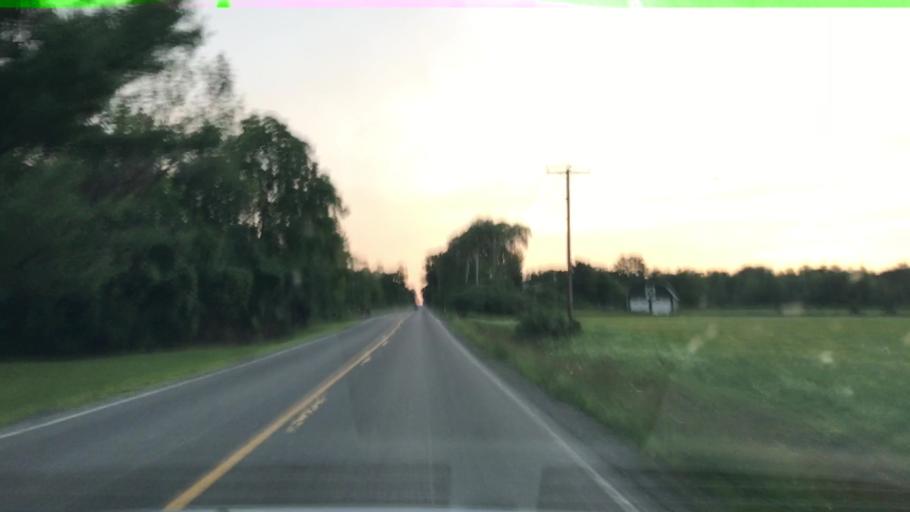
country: US
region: New York
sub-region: Steuben County
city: Sylvan Beach
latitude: 42.5129
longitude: -77.1834
